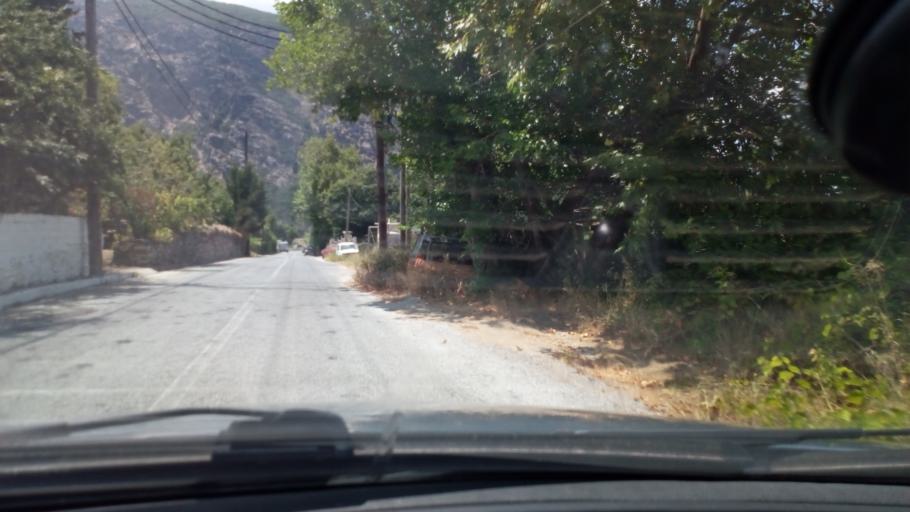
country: GR
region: North Aegean
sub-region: Nomos Samou
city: Agios Kirykos
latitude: 37.6418
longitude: 26.2609
